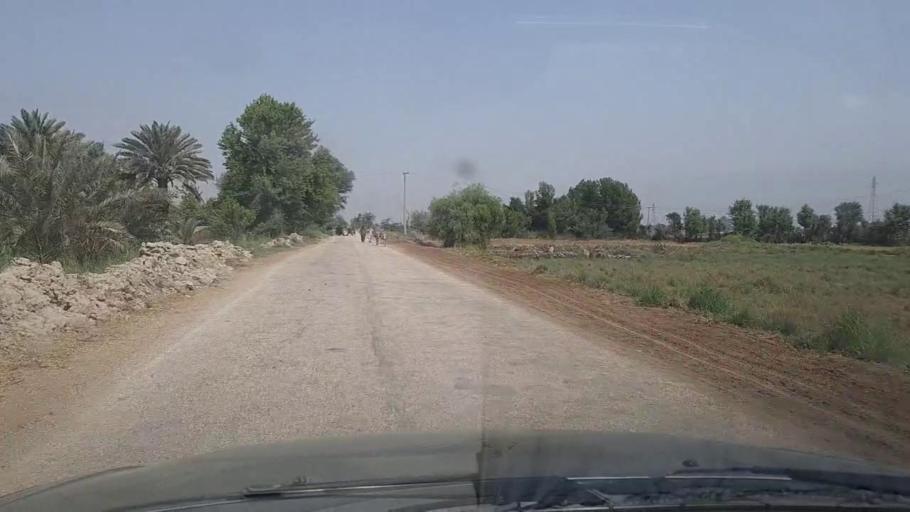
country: PK
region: Sindh
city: Setharja Old
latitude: 27.1436
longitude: 68.5264
